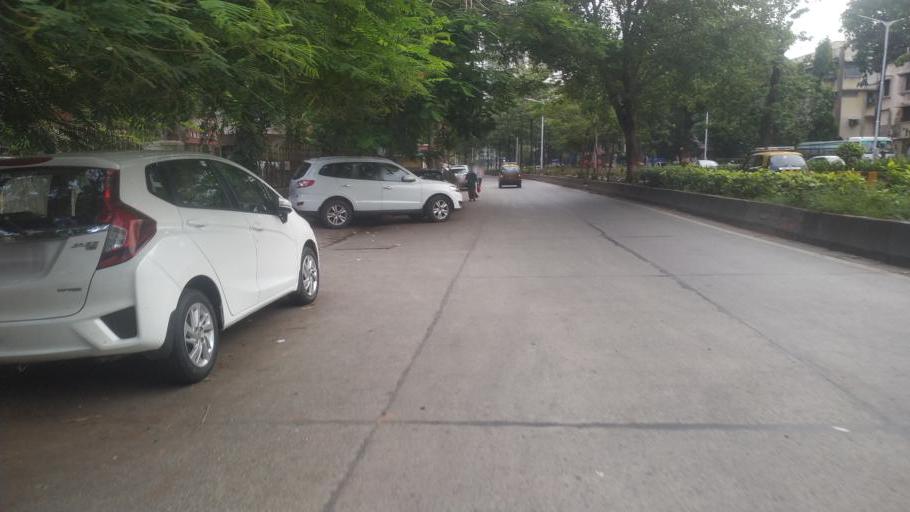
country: IN
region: Maharashtra
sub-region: Mumbai Suburban
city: Mumbai
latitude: 19.0131
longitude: 72.8551
